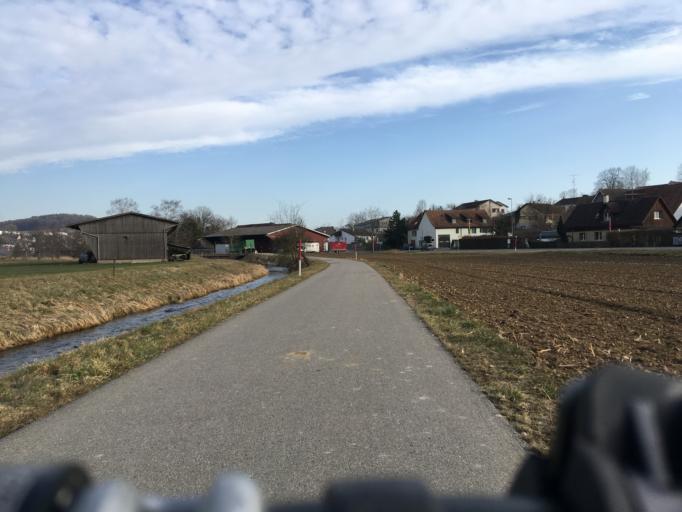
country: CH
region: Schaffhausen
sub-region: Bezirk Reiat
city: Thayngen
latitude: 47.7548
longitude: 8.6930
